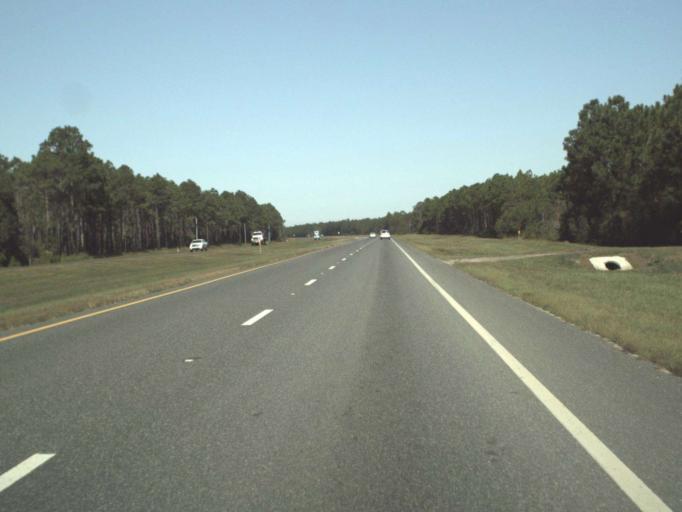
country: US
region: Florida
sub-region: Walton County
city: Seaside
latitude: 30.3254
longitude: -86.0503
